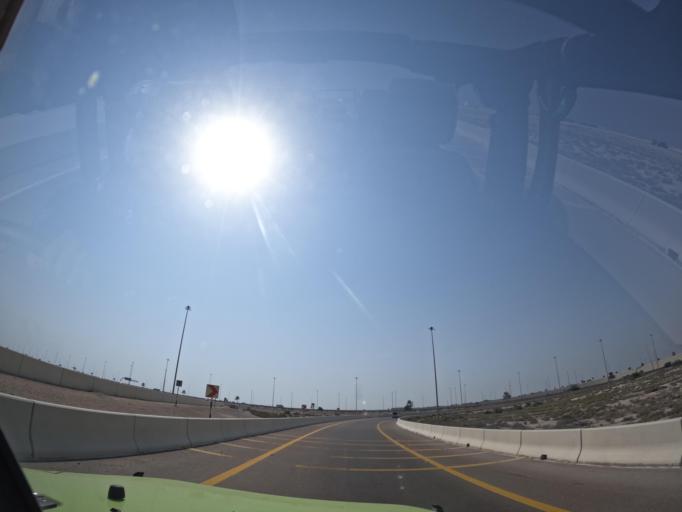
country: AE
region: Abu Dhabi
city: Abu Dhabi
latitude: 24.4050
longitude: 54.6740
